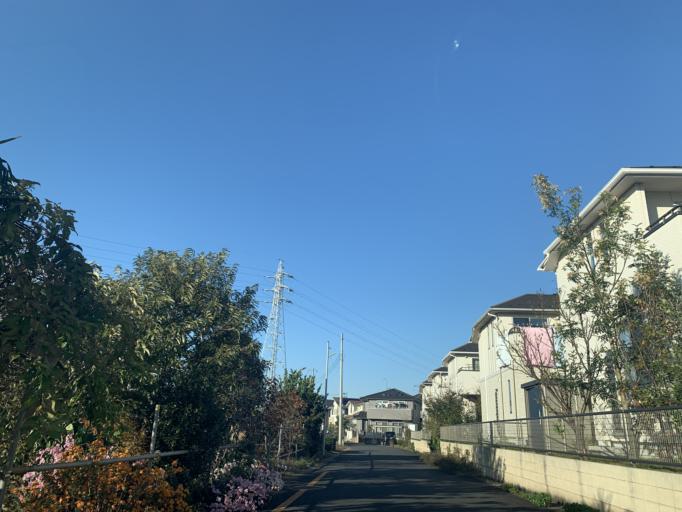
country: JP
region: Chiba
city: Nagareyama
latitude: 35.9010
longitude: 139.9314
